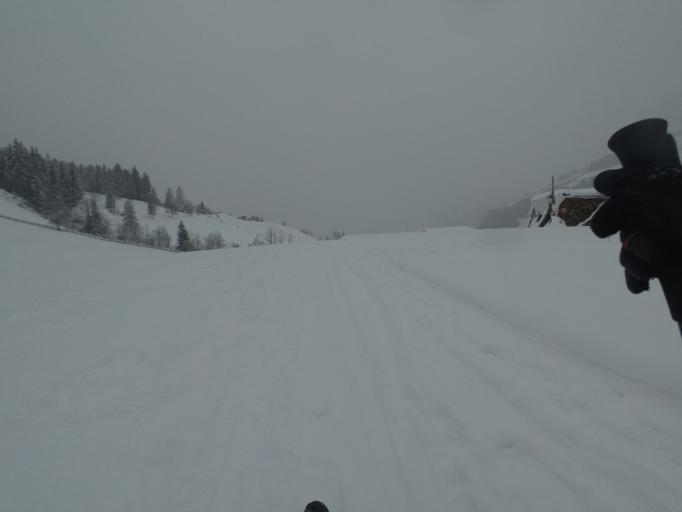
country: AT
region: Salzburg
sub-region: Politischer Bezirk Sankt Johann im Pongau
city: Wagrain
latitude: 47.3305
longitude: 13.2937
